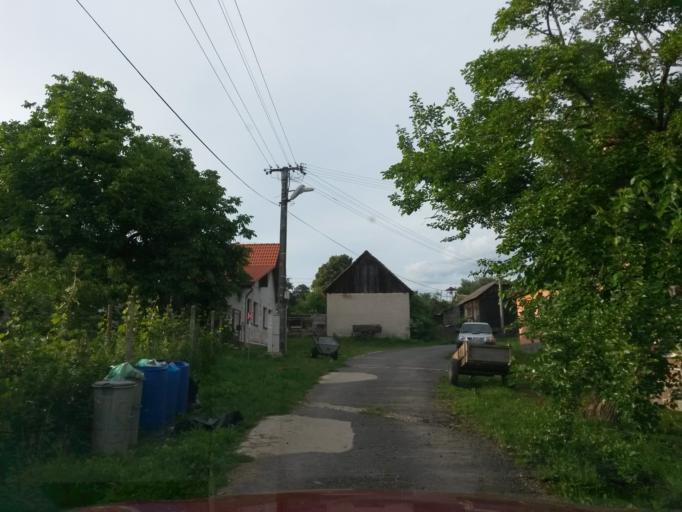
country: SK
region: Banskobystricky
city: Velky Krtis
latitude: 48.3295
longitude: 19.4346
